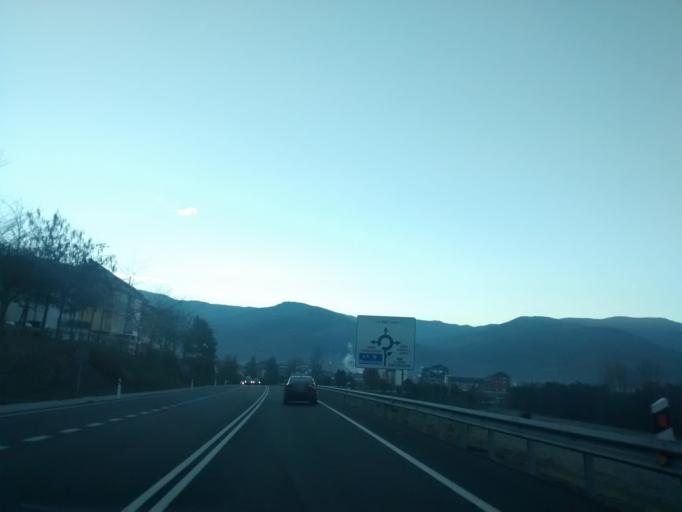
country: ES
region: Catalonia
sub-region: Provincia de Lleida
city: la Seu d'Urgell
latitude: 42.3648
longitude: 1.4553
